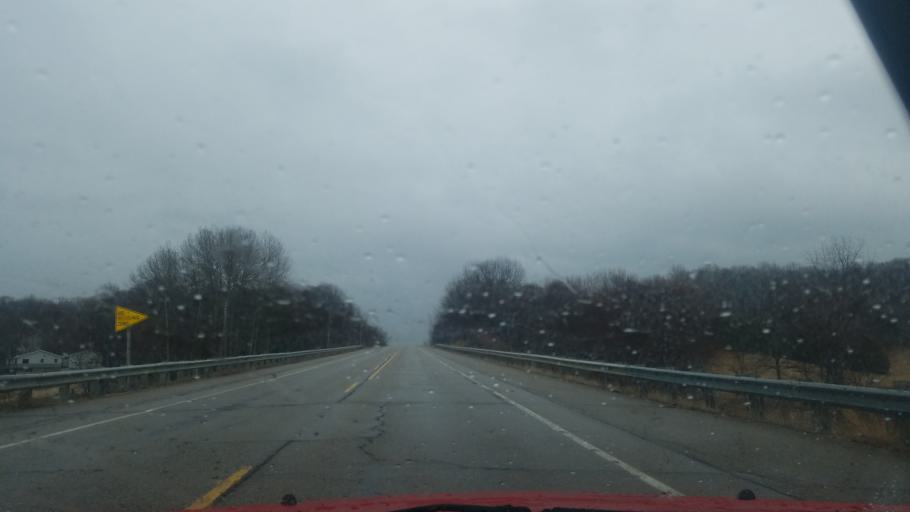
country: US
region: Wisconsin
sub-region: Dunn County
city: Menomonie
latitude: 44.9411
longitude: -91.9191
